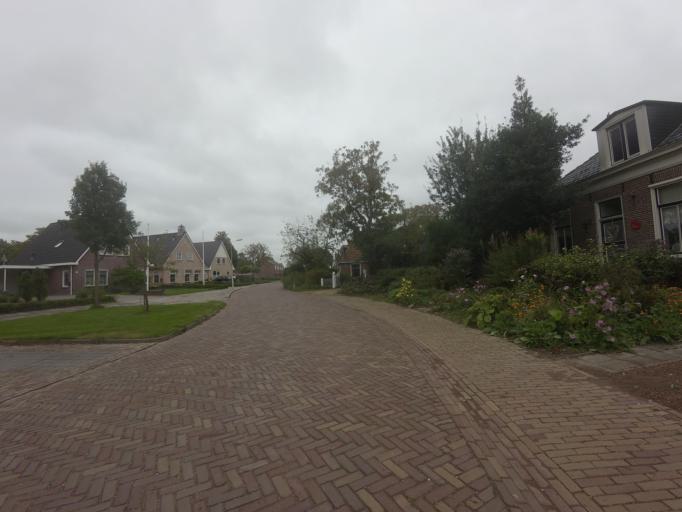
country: NL
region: Friesland
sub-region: Gemeente Ferwerderadiel
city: Ferwert
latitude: 53.3510
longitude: 5.8610
